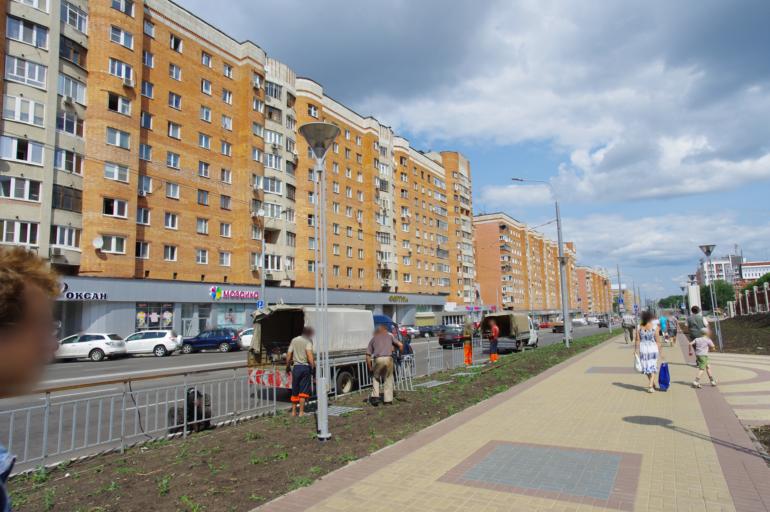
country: RU
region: Nizjnij Novgorod
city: Nizhniy Novgorod
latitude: 56.3139
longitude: 43.9948
